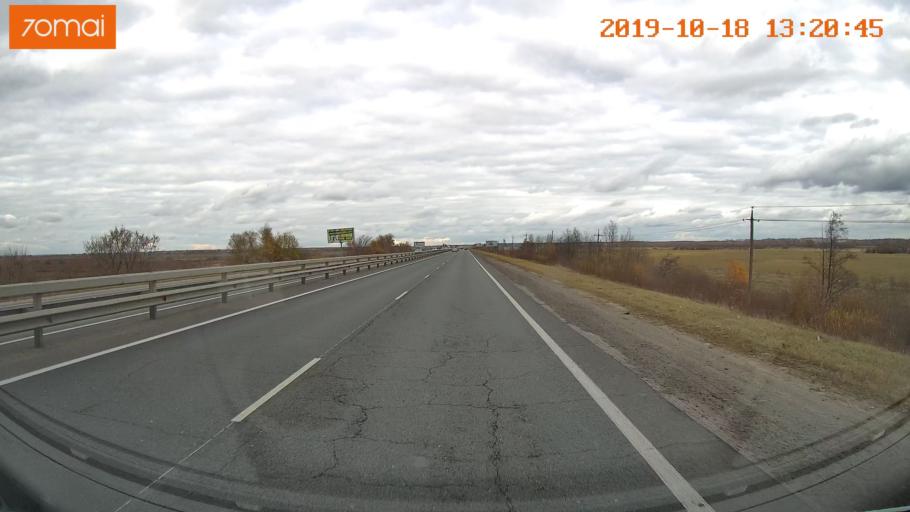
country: RU
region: Rjazan
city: Polyany
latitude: 54.6856
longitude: 39.8344
